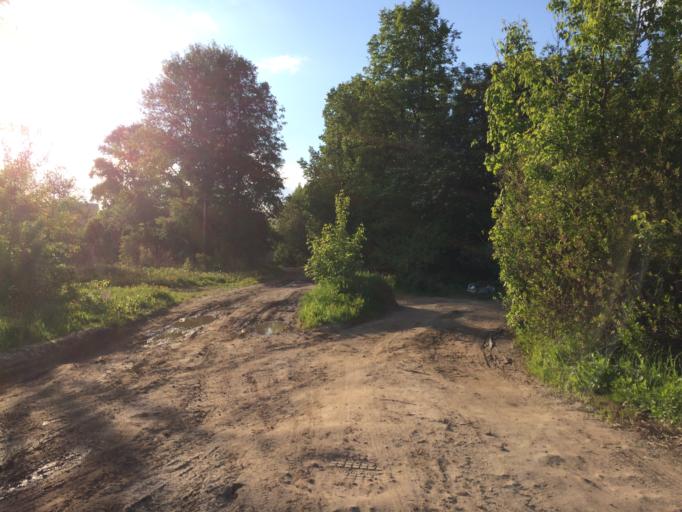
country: RU
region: Mariy-El
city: Yoshkar-Ola
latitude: 56.6315
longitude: 47.9382
